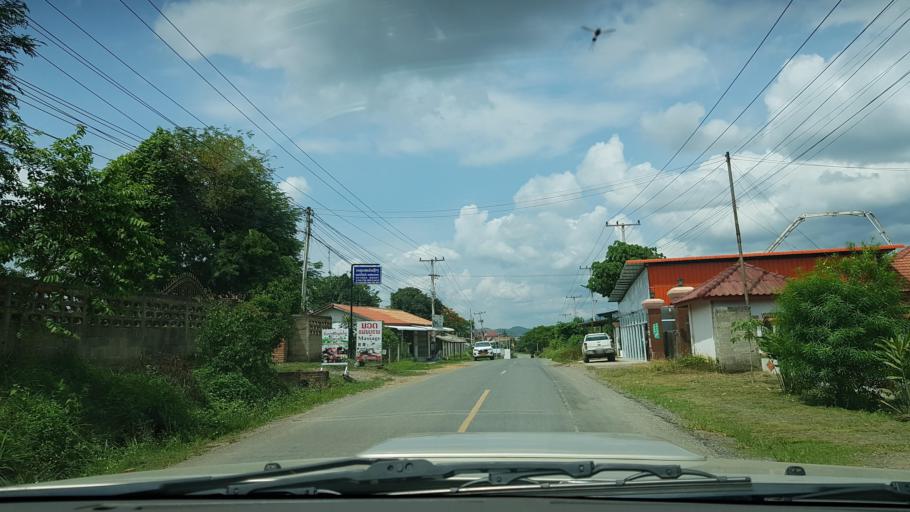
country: LA
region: Loungnamtha
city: Muang Nale
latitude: 20.1376
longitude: 101.4514
